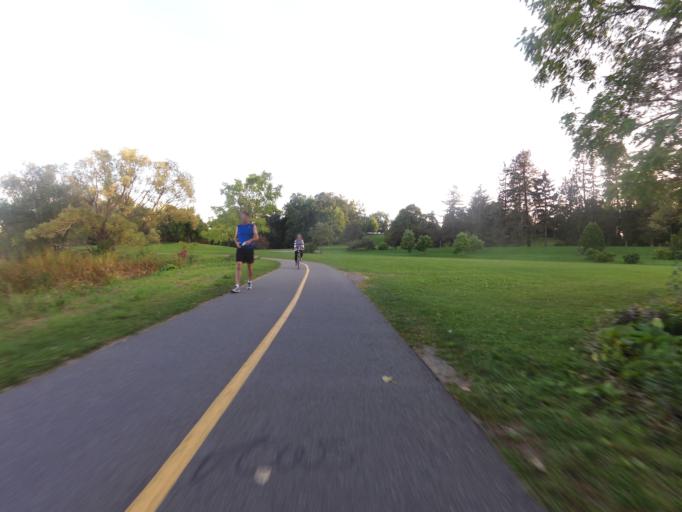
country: CA
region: Ontario
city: Ottawa
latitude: 45.3934
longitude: -75.7041
